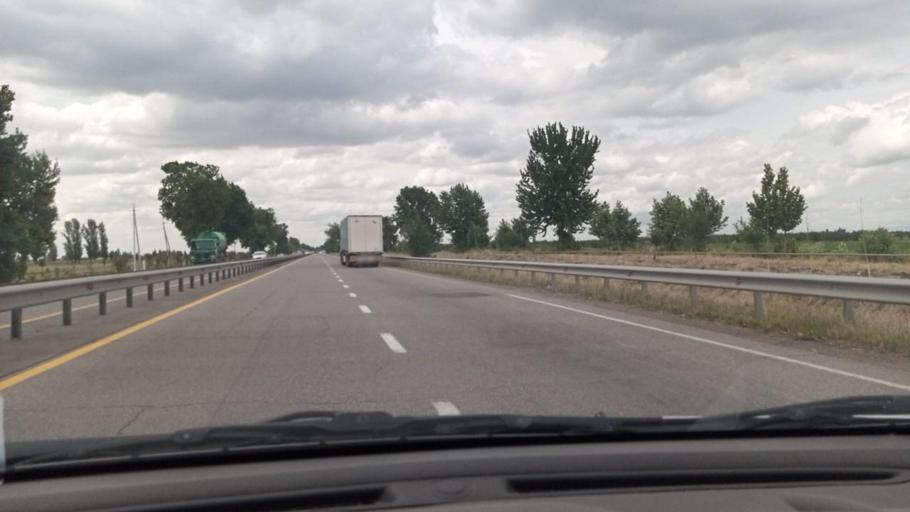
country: UZ
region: Toshkent Shahri
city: Bektemir
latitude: 41.1649
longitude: 69.4179
